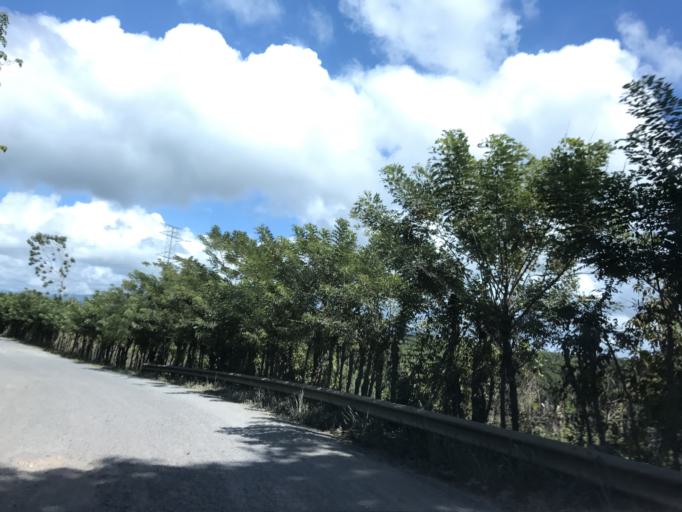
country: GT
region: Izabal
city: Morales
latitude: 15.6400
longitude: -89.0340
